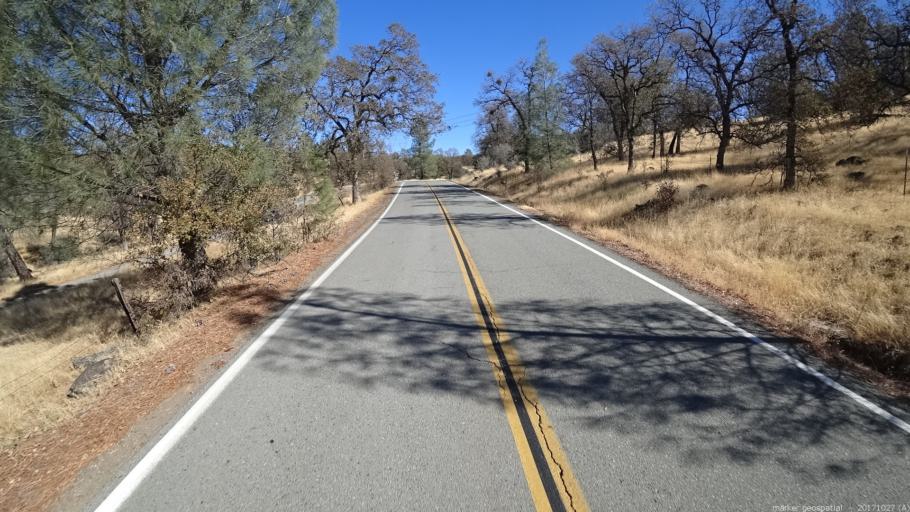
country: US
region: California
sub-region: Shasta County
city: Bella Vista
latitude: 40.7078
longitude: -122.0387
